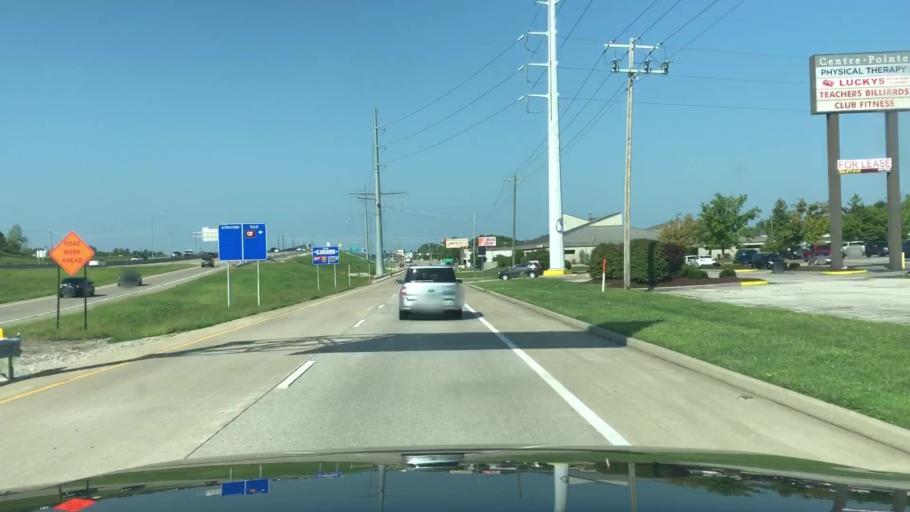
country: US
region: Missouri
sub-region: Saint Charles County
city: Saint Peters
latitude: 38.7485
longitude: -90.5865
